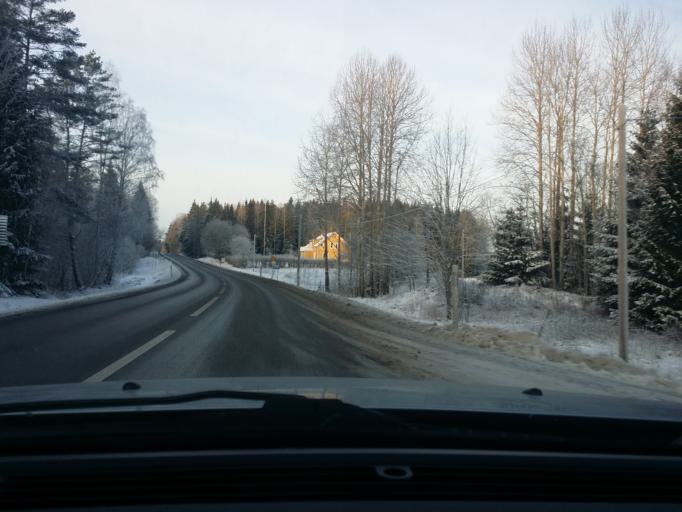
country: SE
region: OErebro
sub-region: Lindesbergs Kommun
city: Frovi
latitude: 59.5062
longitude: 15.3709
